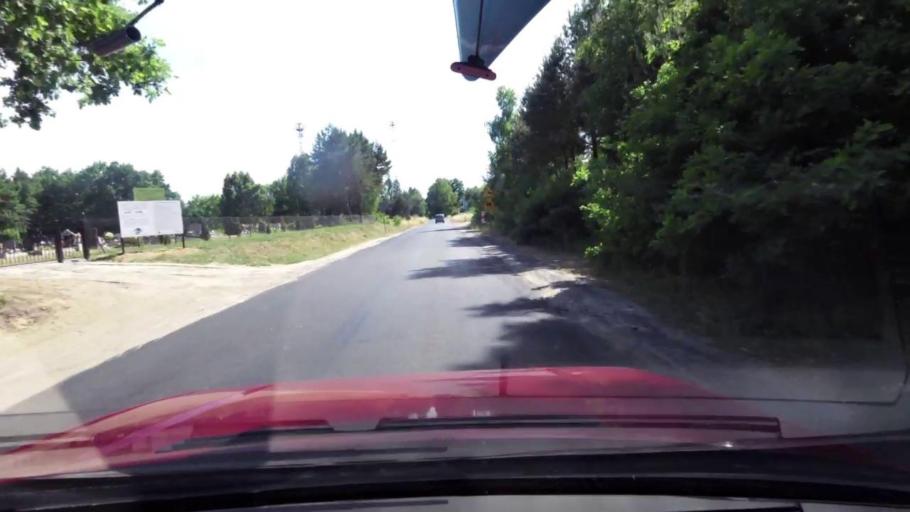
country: PL
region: Pomeranian Voivodeship
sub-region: Powiat slupski
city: Kepice
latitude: 54.2863
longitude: 16.9590
